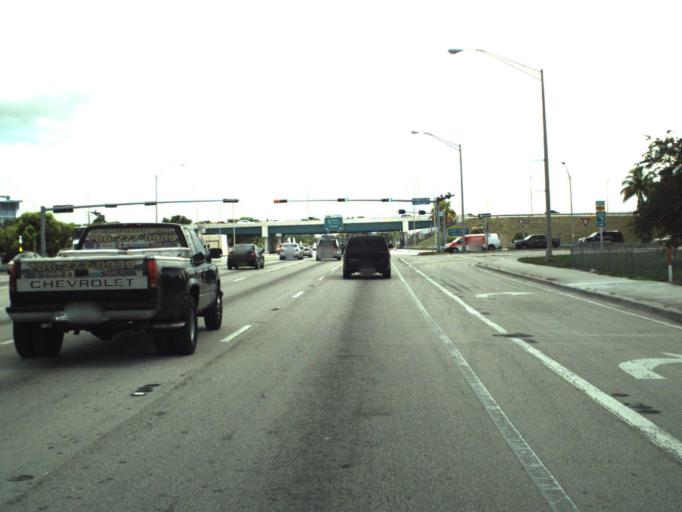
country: US
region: Florida
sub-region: Miami-Dade County
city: Lake Lucerne
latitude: 25.9750
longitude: -80.2471
